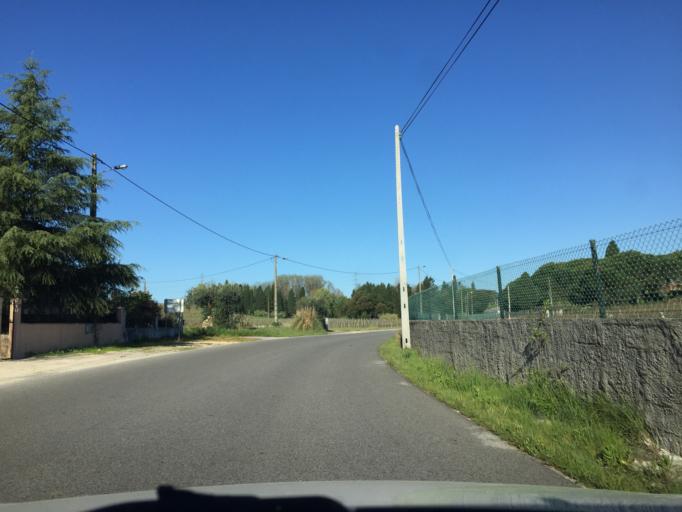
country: PT
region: Aveiro
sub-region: Anadia
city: Arcos
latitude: 40.4506
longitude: -8.4718
